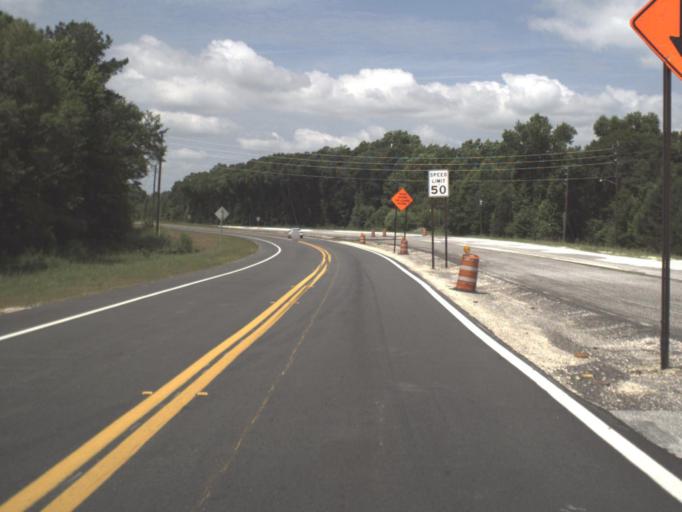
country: US
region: Florida
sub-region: Nassau County
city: Callahan
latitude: 30.5567
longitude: -81.8379
